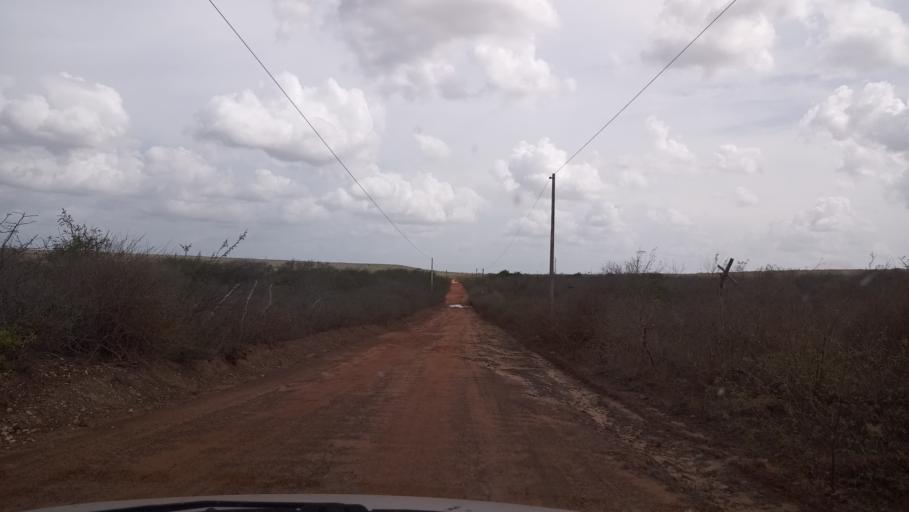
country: BR
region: Rio Grande do Norte
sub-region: Joao Camara
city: Joao Camara
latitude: -5.4717
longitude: -35.8275
